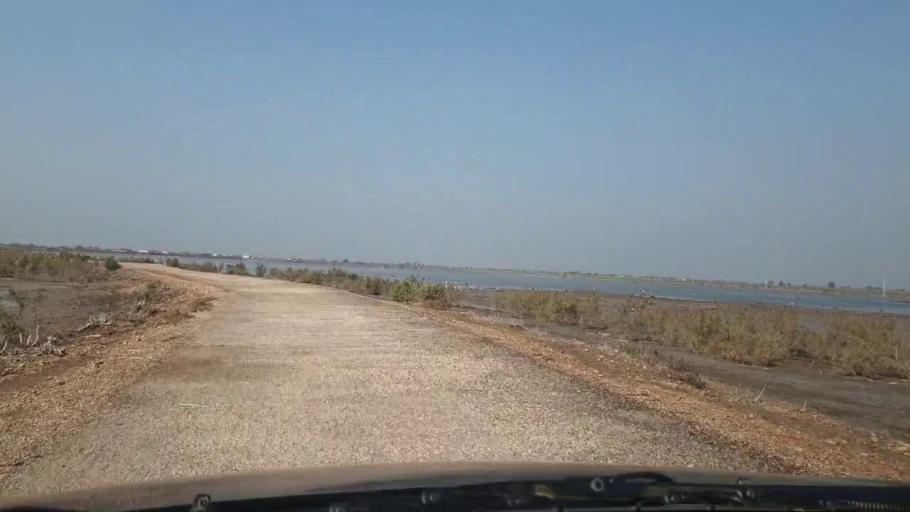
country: PK
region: Sindh
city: Jhol
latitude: 25.9018
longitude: 69.0072
